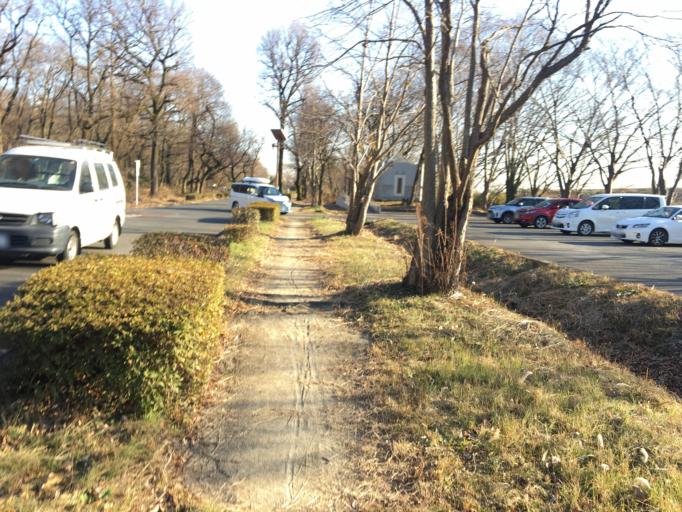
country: JP
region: Saitama
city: Shiki
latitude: 35.8564
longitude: 139.5934
